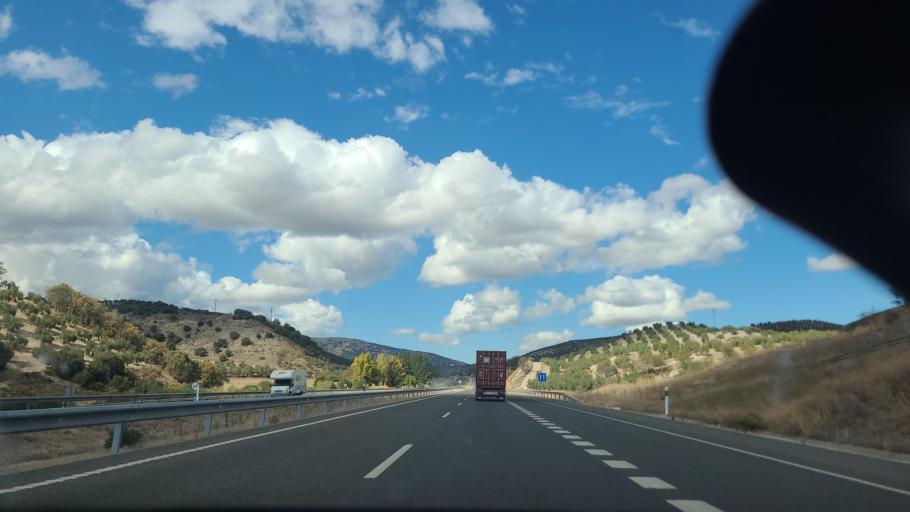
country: ES
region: Andalusia
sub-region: Provincia de Granada
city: Campotejar
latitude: 37.4987
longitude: -3.6267
